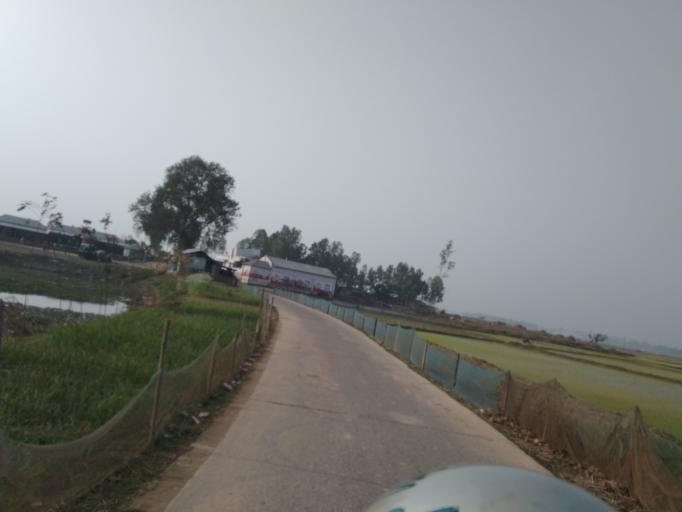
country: BD
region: Rajshahi
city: Ishurdi
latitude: 24.4921
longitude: 89.2024
